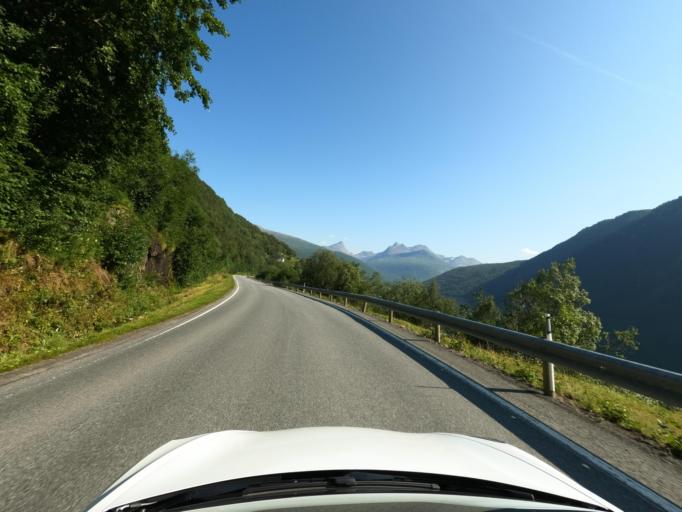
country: NO
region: Nordland
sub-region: Narvik
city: Narvik
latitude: 68.3906
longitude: 17.5417
